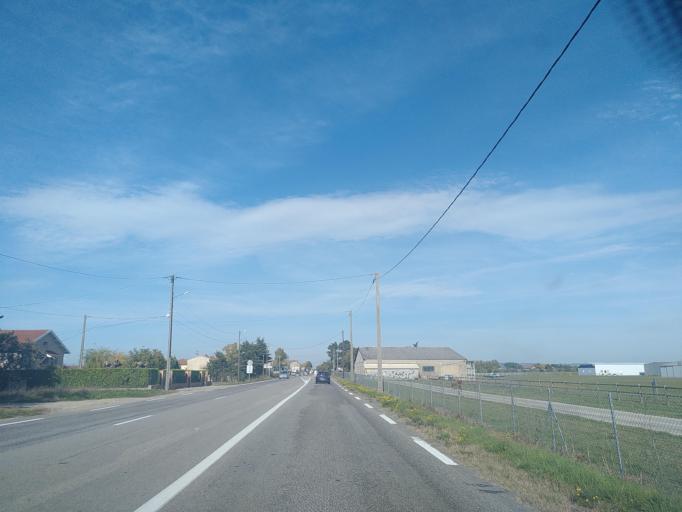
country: FR
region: Rhone-Alpes
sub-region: Departement de la Drome
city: Andancette
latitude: 45.2542
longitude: 4.8224
